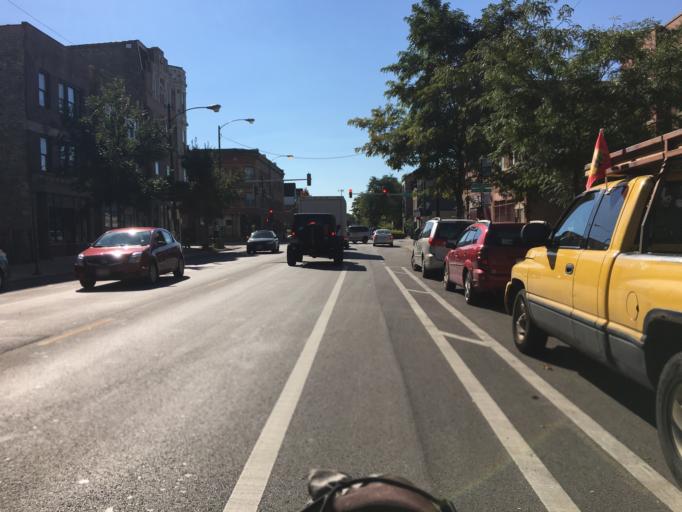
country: US
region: Illinois
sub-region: Cook County
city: Chicago
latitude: 41.8999
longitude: -87.6969
